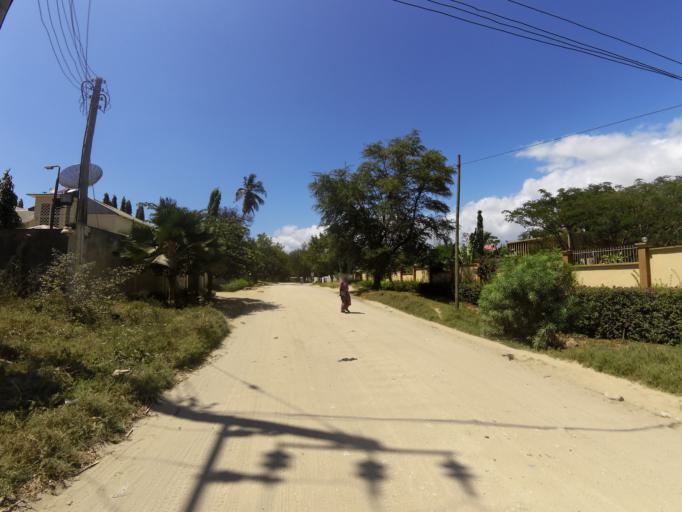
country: TZ
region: Dar es Salaam
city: Magomeni
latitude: -6.7925
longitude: 39.2725
